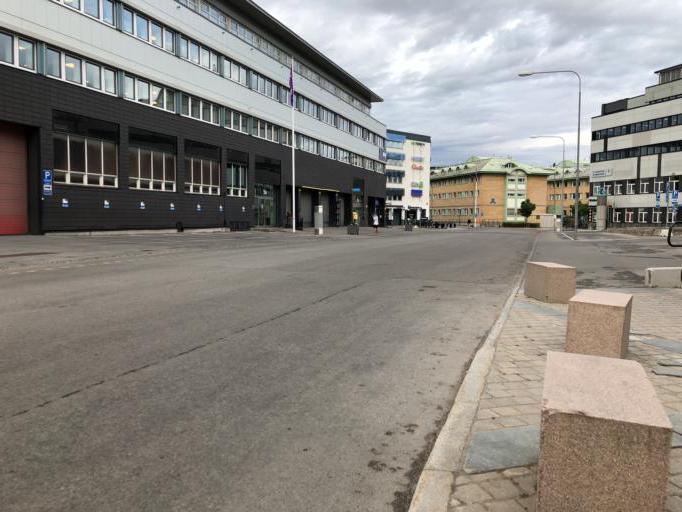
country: SE
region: Stockholm
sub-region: Sundbybergs Kommun
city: Sundbyberg
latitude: 59.3601
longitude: 17.9787
